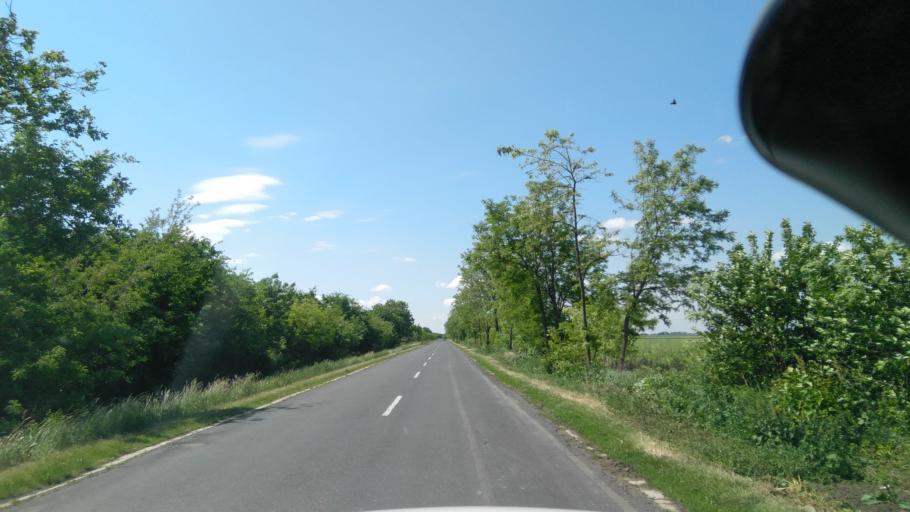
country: HU
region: Bekes
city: Medgyesegyhaza
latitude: 46.4822
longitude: 21.0226
